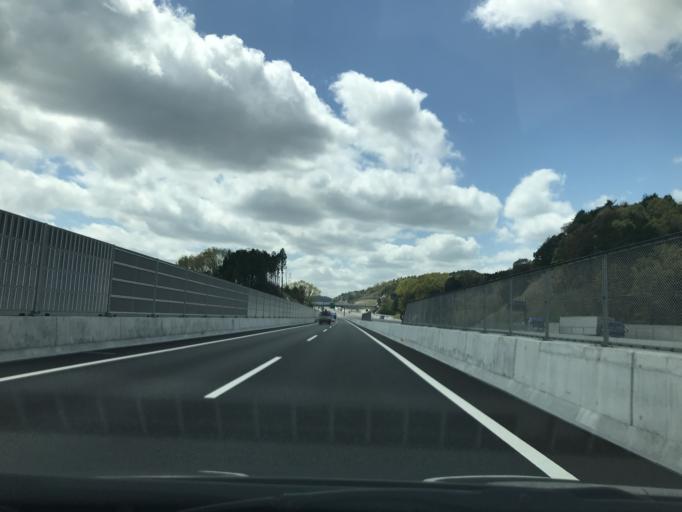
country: JP
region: Osaka
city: Ibaraki
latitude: 34.8894
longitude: 135.5411
